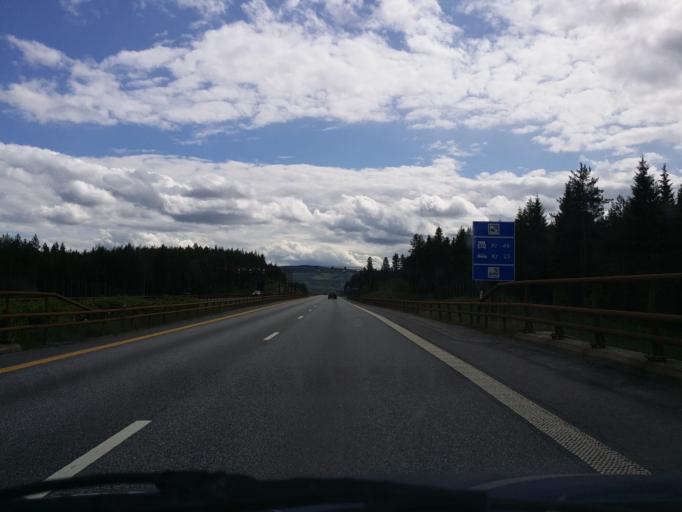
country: NO
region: Hedmark
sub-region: Stange
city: Stange
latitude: 60.6508
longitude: 11.2921
